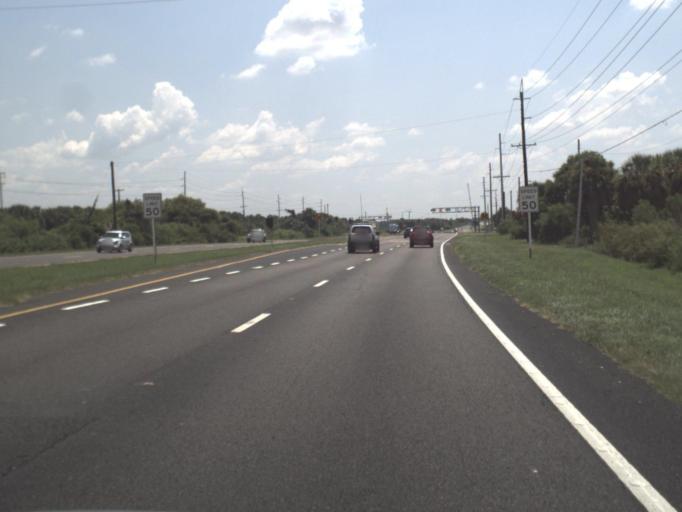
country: US
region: Florida
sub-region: Hillsborough County
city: Gibsonton
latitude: 27.8688
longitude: -82.3874
